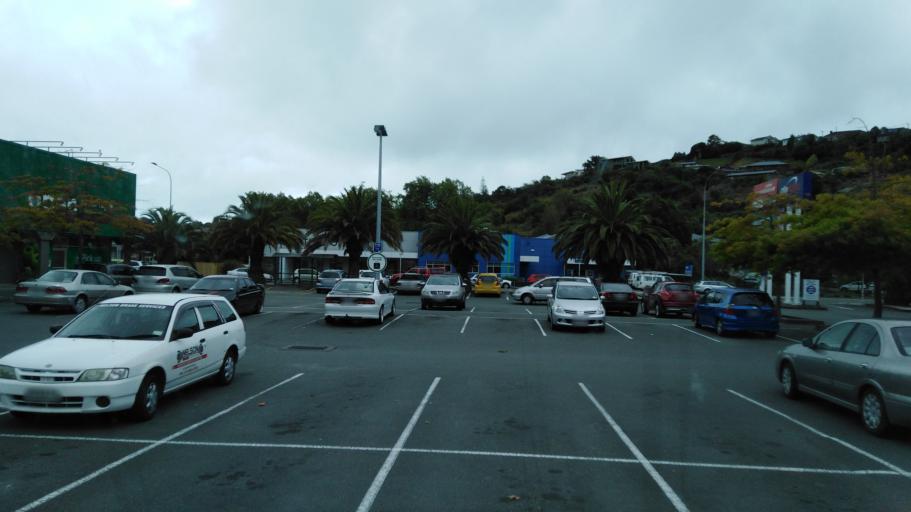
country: NZ
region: Nelson
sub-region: Nelson City
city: Nelson
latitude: -41.2725
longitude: 173.2782
